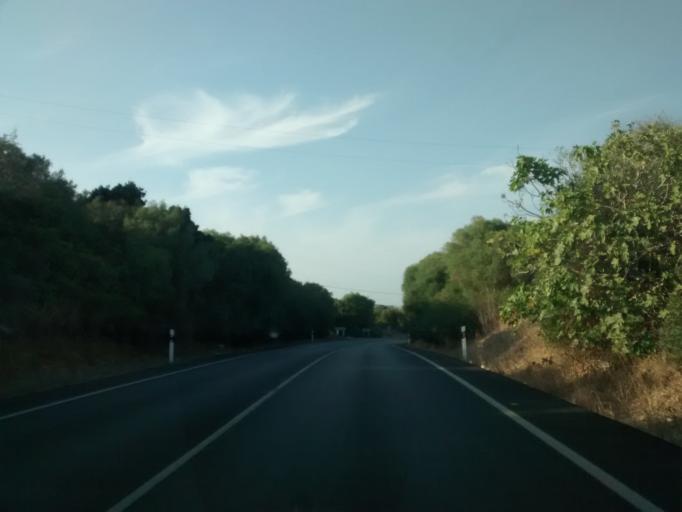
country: ES
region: Andalusia
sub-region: Provincia de Cadiz
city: Vejer de la Frontera
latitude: 36.2382
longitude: -5.9515
